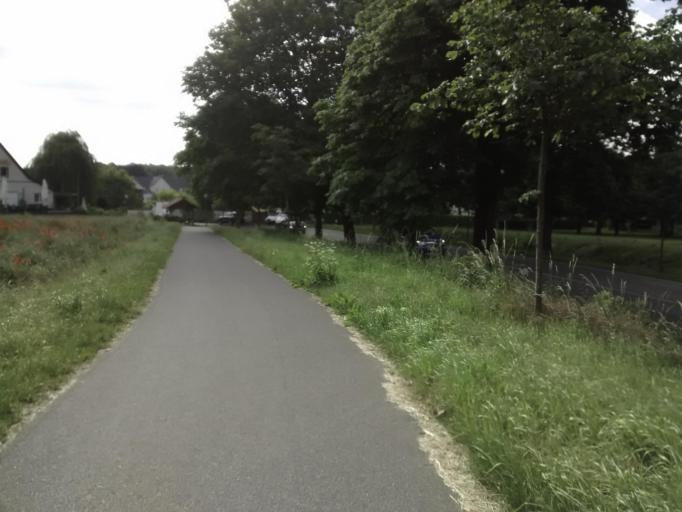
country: DE
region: Brandenburg
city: Glienicke
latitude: 52.6564
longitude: 13.3358
